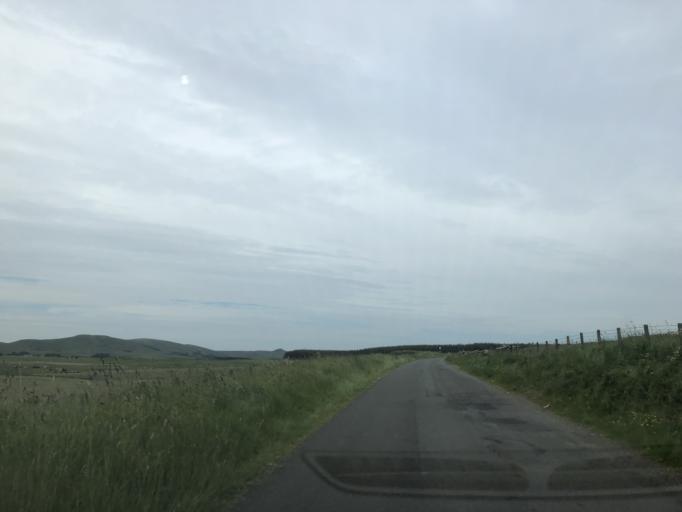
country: GB
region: Scotland
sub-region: The Scottish Borders
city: West Linton
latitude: 55.7661
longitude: -3.3236
